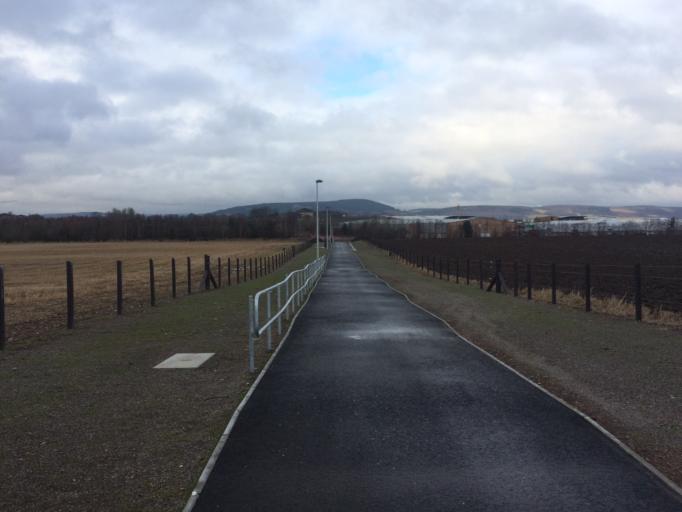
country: GB
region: Scotland
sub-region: Highland
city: Inverness
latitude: 57.4777
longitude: -4.1756
